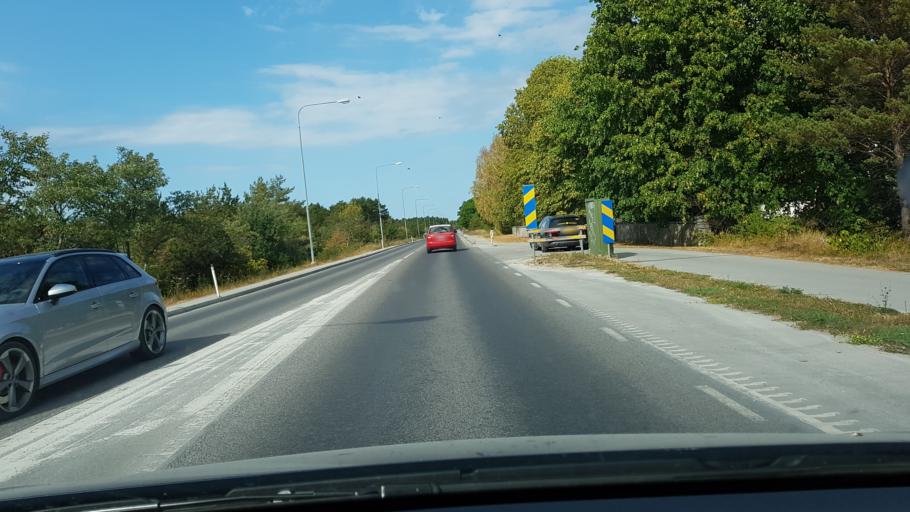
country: SE
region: Gotland
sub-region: Gotland
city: Visby
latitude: 57.6522
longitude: 18.3182
